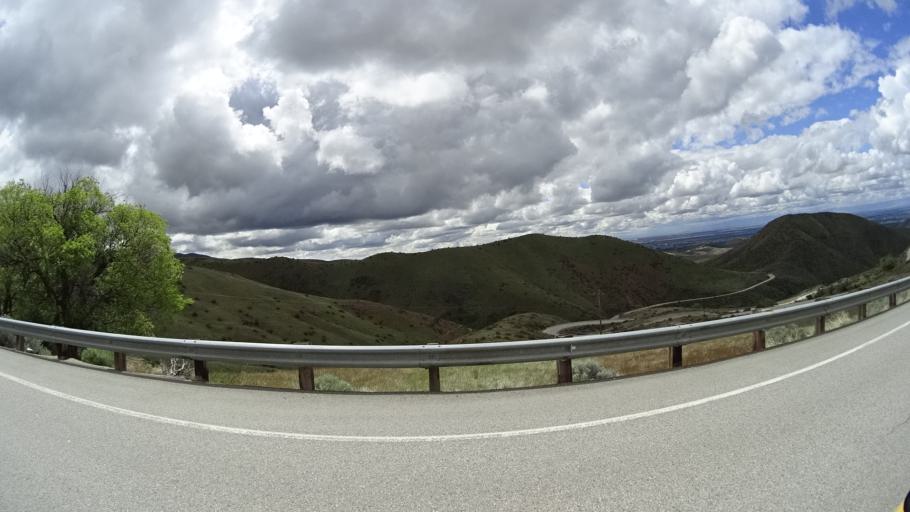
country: US
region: Idaho
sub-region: Ada County
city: Boise
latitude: 43.6926
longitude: -116.1790
